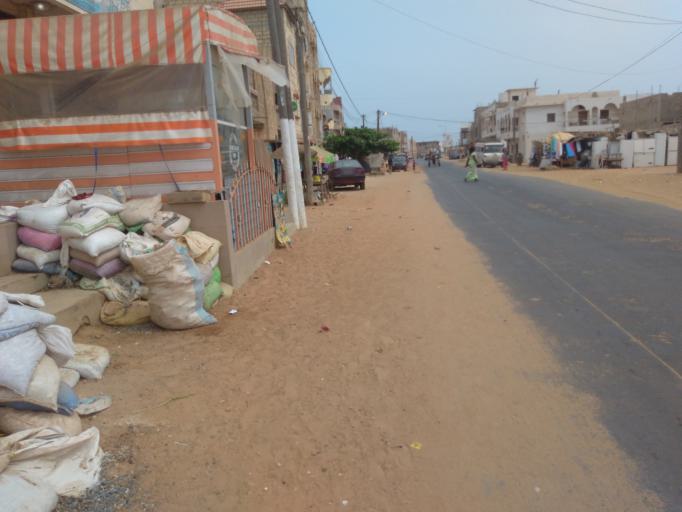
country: SN
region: Dakar
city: Pikine
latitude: 14.8004
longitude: -17.3375
